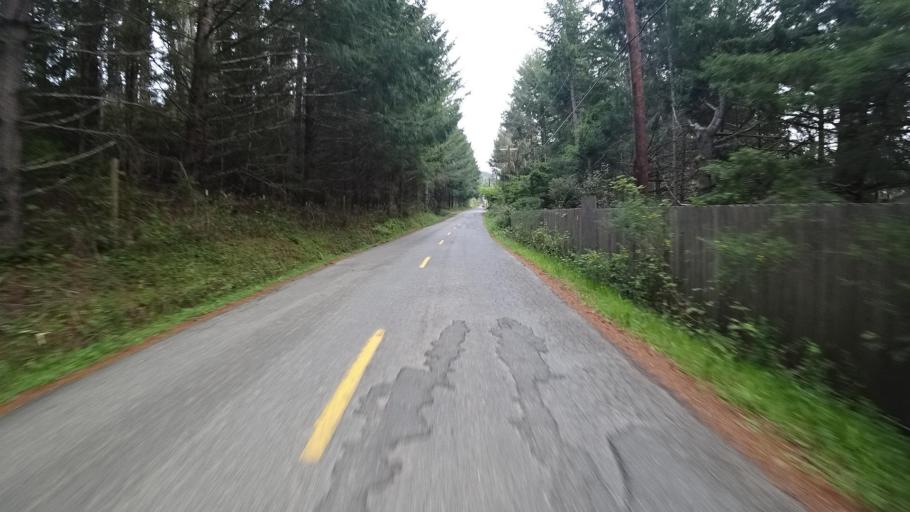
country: US
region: California
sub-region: Humboldt County
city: Redway
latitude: 40.2950
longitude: -123.8202
